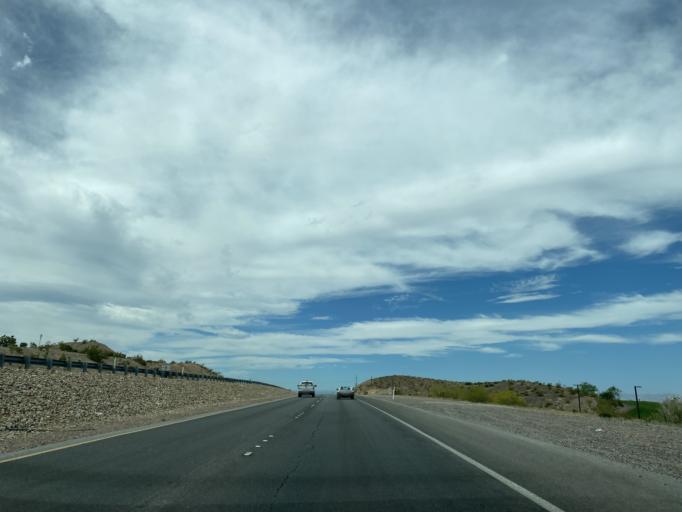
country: US
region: Nevada
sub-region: Clark County
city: Henderson
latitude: 36.0829
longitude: -114.9275
